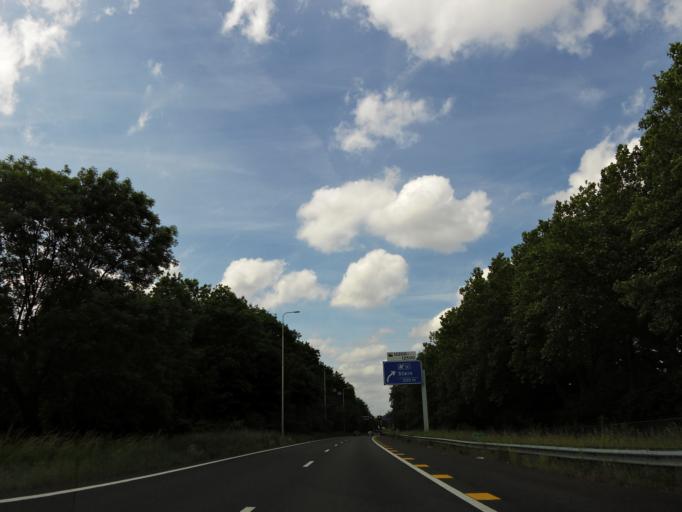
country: NL
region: Limburg
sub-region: Gemeente Stein
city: Stein
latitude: 50.9670
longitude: 5.7926
